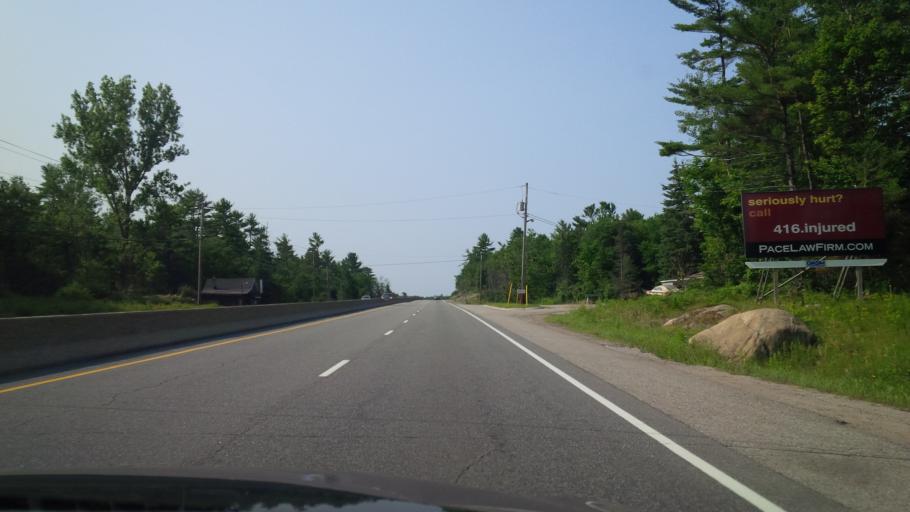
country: CA
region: Ontario
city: Gravenhurst
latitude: 44.8284
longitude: -79.3217
